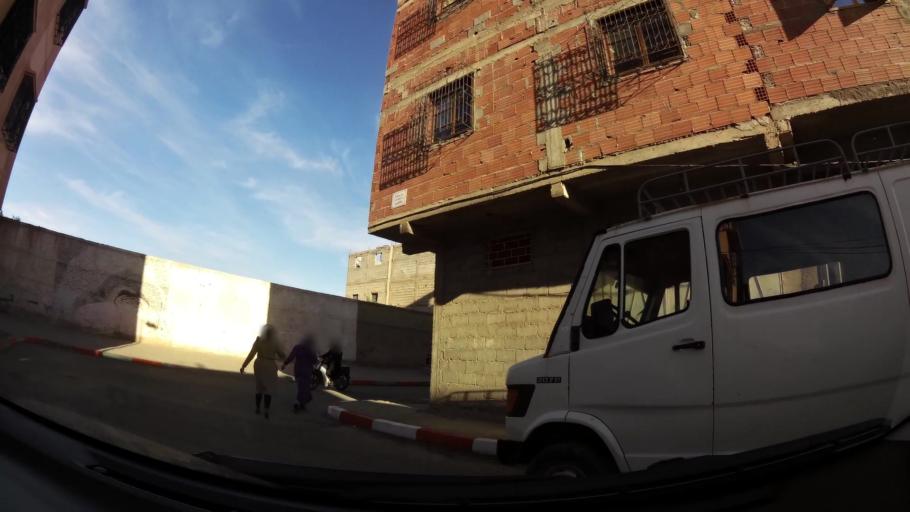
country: MA
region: Marrakech-Tensift-Al Haouz
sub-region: Marrakech
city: Marrakesh
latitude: 31.6174
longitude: -8.0691
